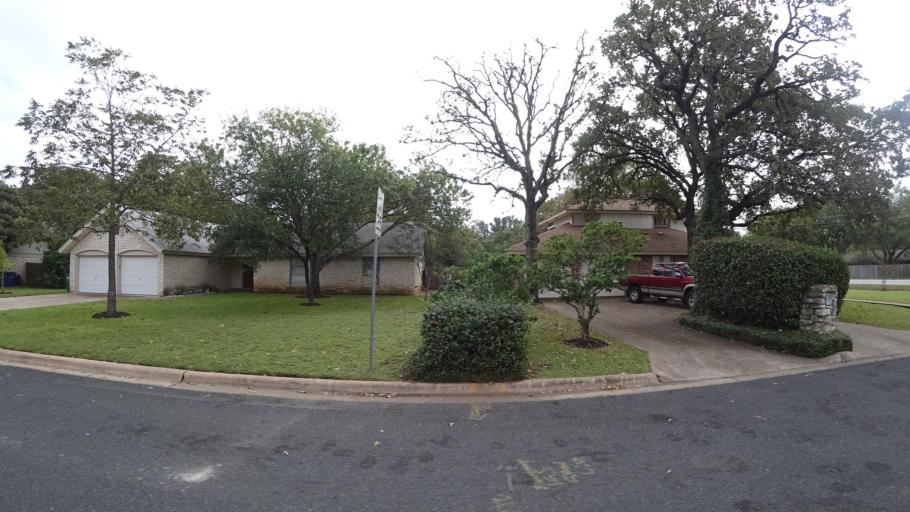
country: US
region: Texas
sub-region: Travis County
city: Shady Hollow
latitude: 30.2135
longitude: -97.8381
